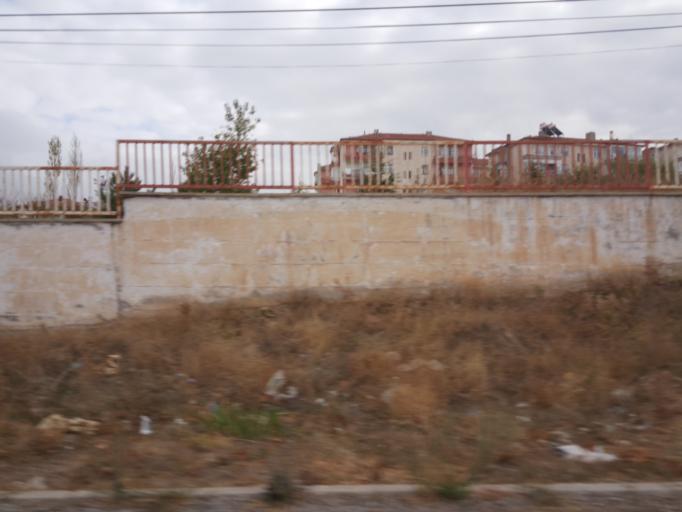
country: TR
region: Kirikkale
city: Keskin
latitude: 39.6780
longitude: 33.5992
